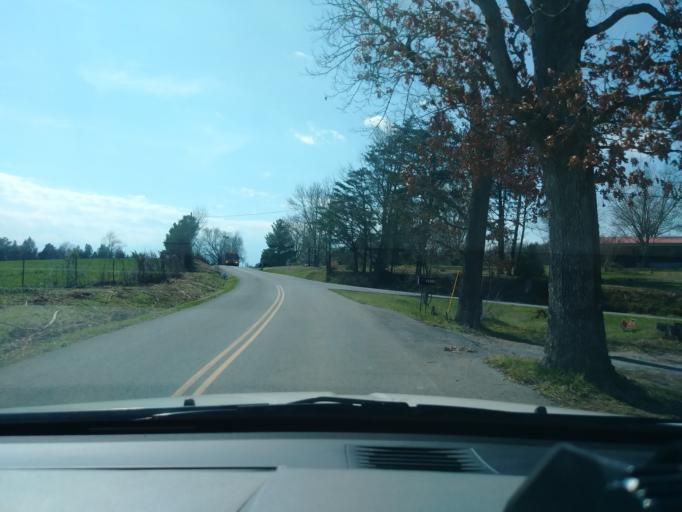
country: US
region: Tennessee
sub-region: Greene County
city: Greeneville
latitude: 36.0686
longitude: -82.7845
